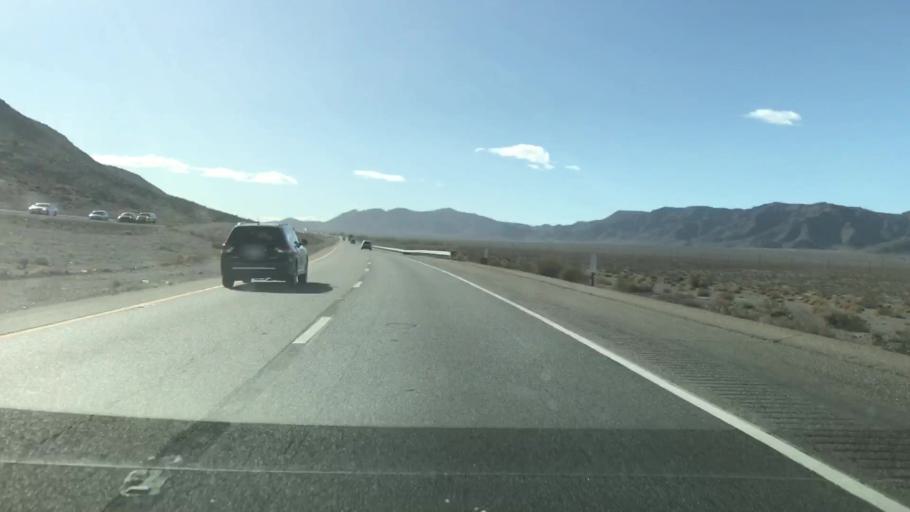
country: US
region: California
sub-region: San Bernardino County
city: Fort Irwin
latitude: 35.1936
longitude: -116.1539
